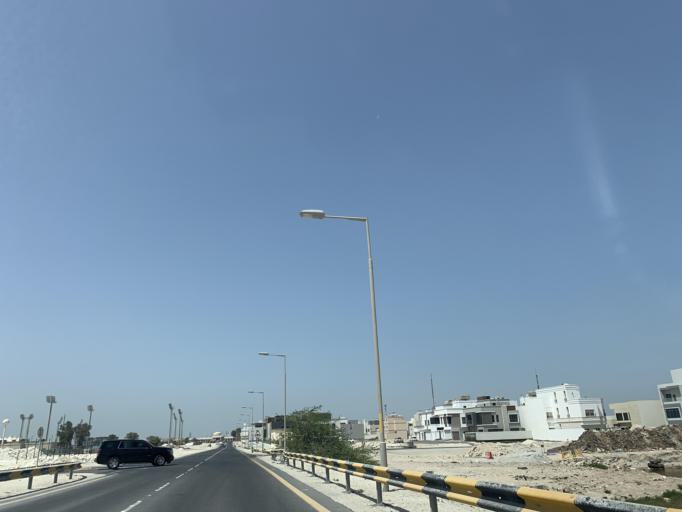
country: BH
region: Northern
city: Ar Rifa'
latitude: 26.1503
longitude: 50.5487
